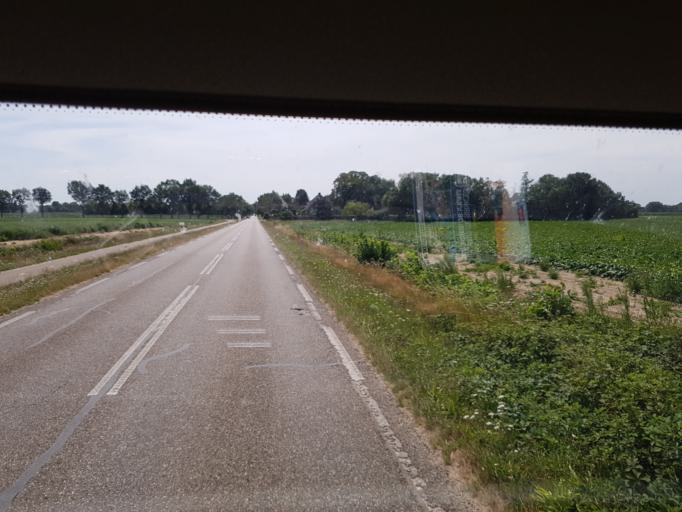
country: NL
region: Limburg
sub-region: Gemeente Leudal
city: Kelpen-Oler
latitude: 51.2039
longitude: 5.8062
